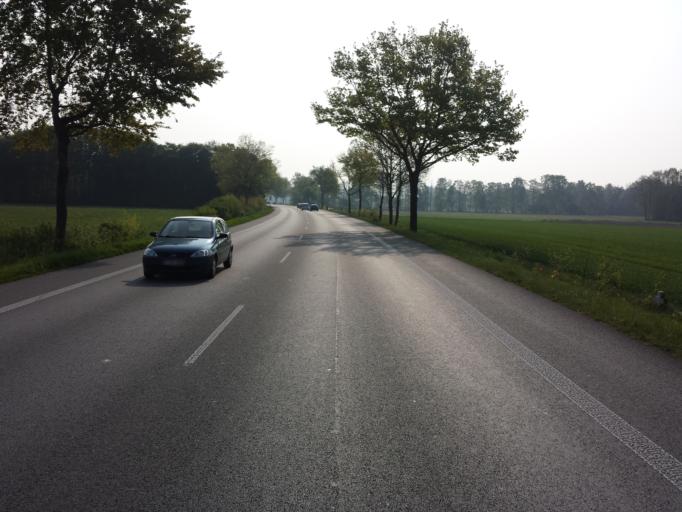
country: DE
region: North Rhine-Westphalia
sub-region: Regierungsbezirk Detmold
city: Guetersloh
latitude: 51.9222
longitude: 8.3344
